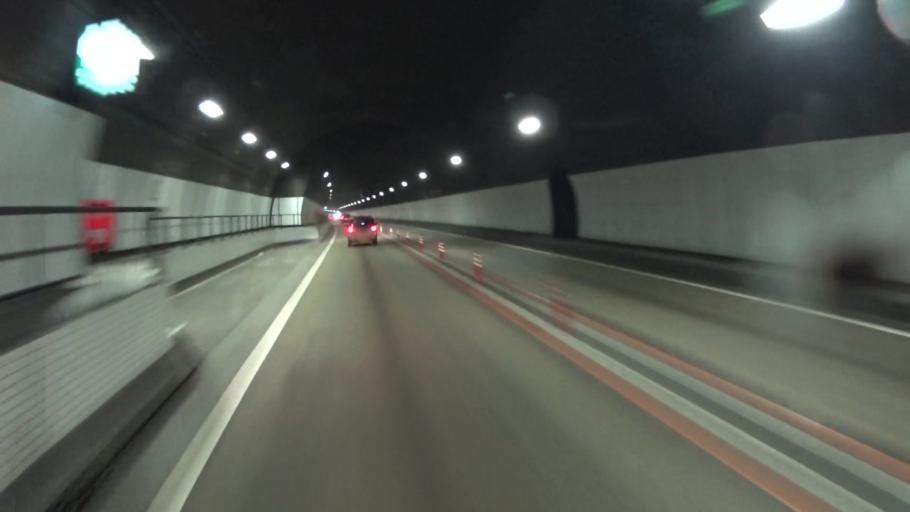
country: JP
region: Kyoto
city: Kameoka
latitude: 35.1378
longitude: 135.4508
